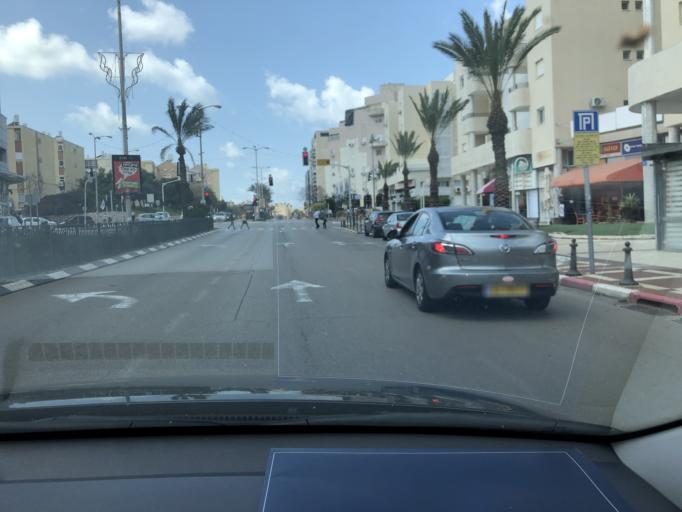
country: IL
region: Haifa
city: Hadera
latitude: 32.4409
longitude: 34.9156
